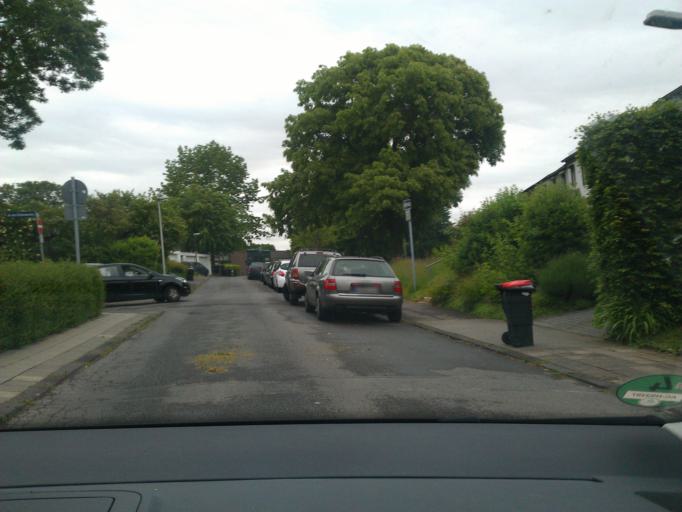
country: DE
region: North Rhine-Westphalia
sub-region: Regierungsbezirk Koln
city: Aachen
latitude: 50.7609
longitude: 6.1083
